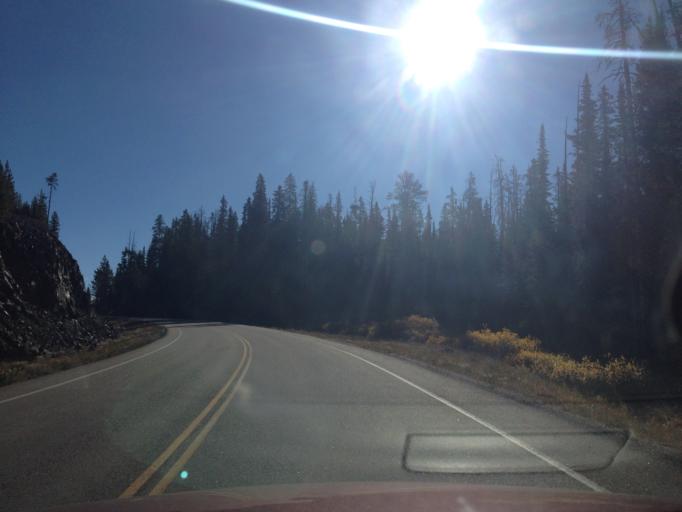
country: US
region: Montana
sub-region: Carbon County
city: Red Lodge
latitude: 45.0267
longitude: -109.8945
